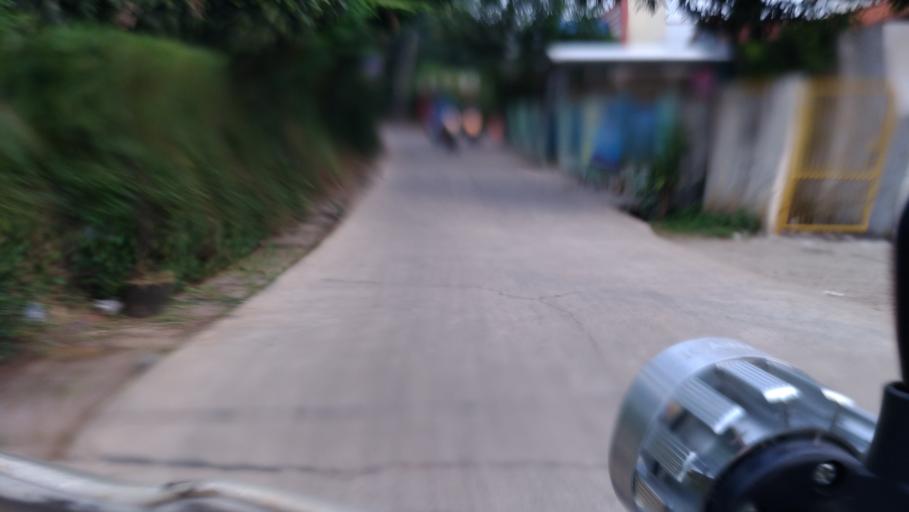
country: ID
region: West Java
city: Depok
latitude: -6.3567
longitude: 106.8701
